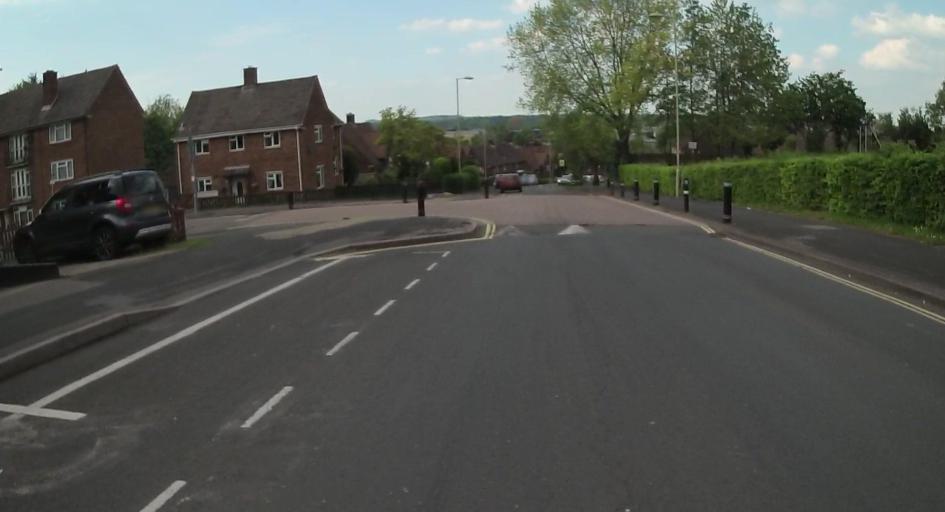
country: GB
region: England
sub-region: Hampshire
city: Winchester
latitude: 51.0629
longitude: -1.2994
